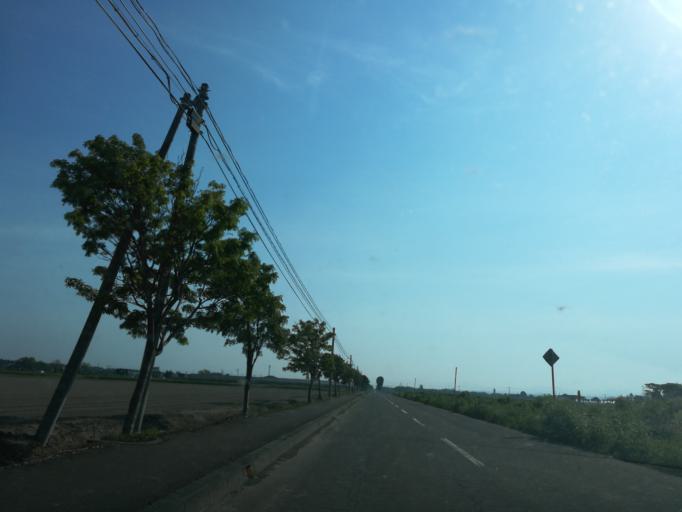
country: JP
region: Hokkaido
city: Iwamizawa
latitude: 43.1649
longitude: 141.6943
